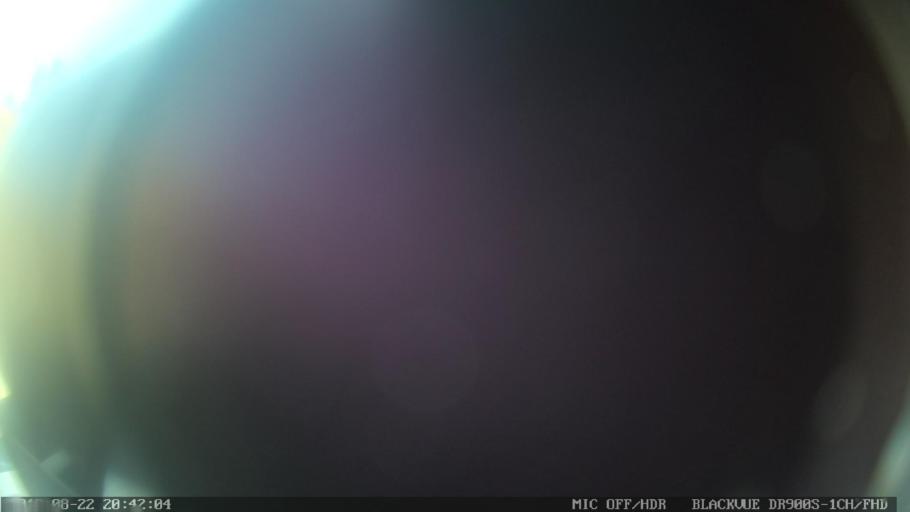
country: PT
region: Castelo Branco
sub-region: Proenca-A-Nova
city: Proenca-a-Nova
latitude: 39.6916
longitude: -7.8118
